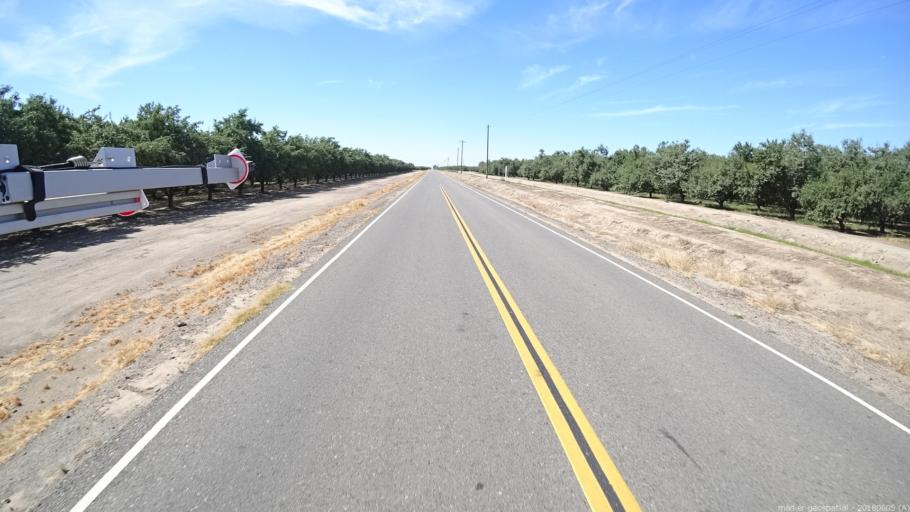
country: US
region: California
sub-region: Madera County
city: Chowchilla
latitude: 37.0609
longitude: -120.3830
